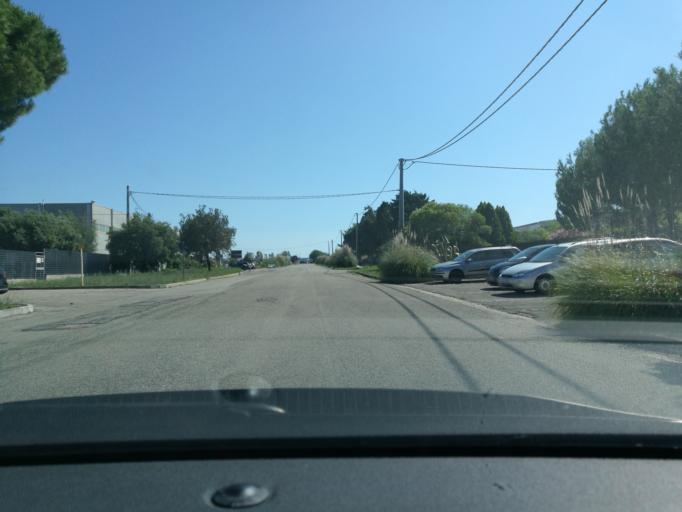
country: IT
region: Abruzzo
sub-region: Provincia di Chieti
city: Vasto
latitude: 42.1718
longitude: 14.6969
